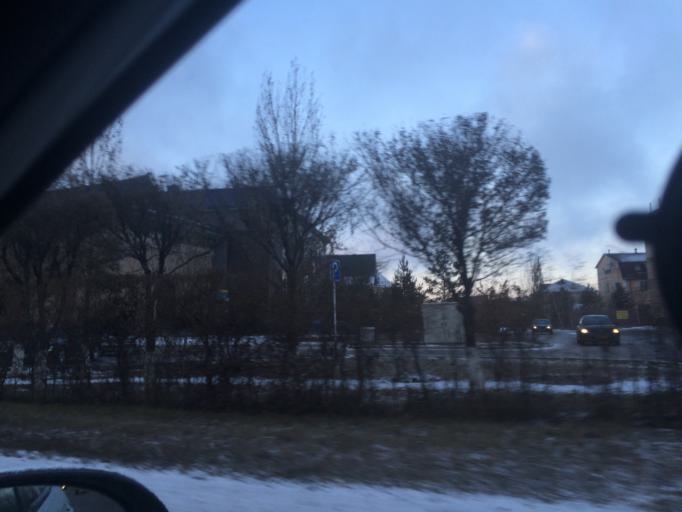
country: KZ
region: Astana Qalasy
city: Astana
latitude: 51.1423
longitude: 71.4105
